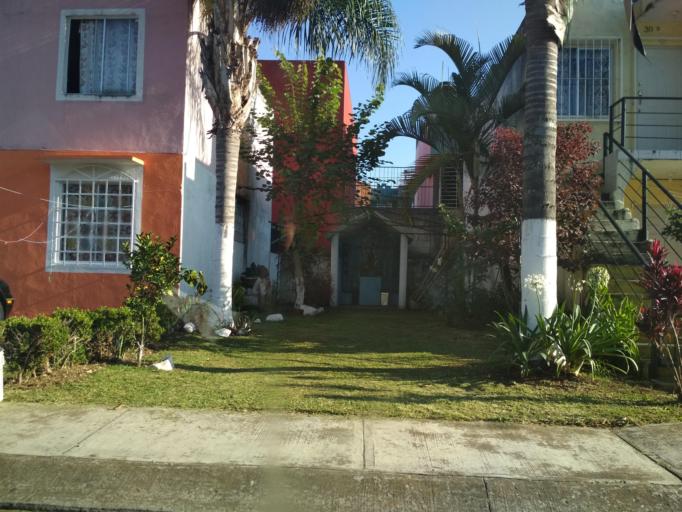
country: MX
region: Veracruz
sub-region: Fortin
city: Fraccionamiento Villas de la Llave
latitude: 18.9188
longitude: -96.9932
